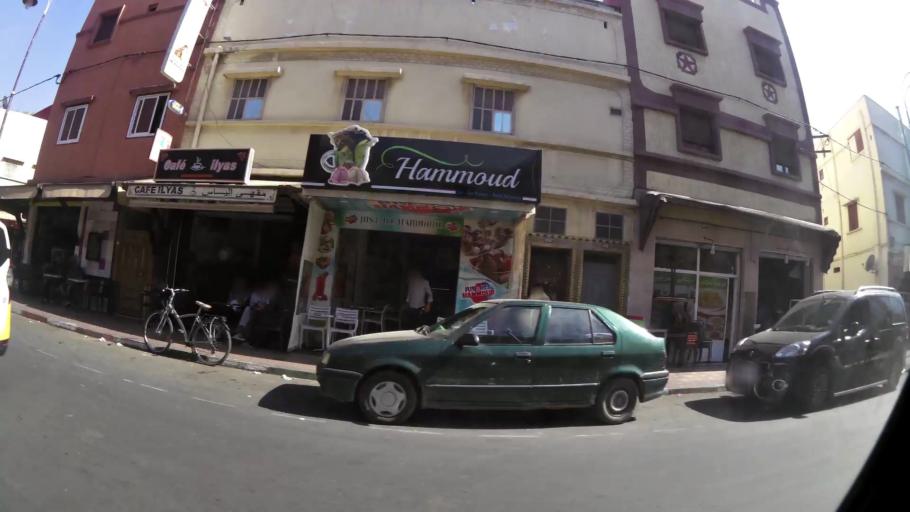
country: MA
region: Souss-Massa-Draa
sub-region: Inezgane-Ait Mellou
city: Inezgane
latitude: 30.3712
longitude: -9.5340
